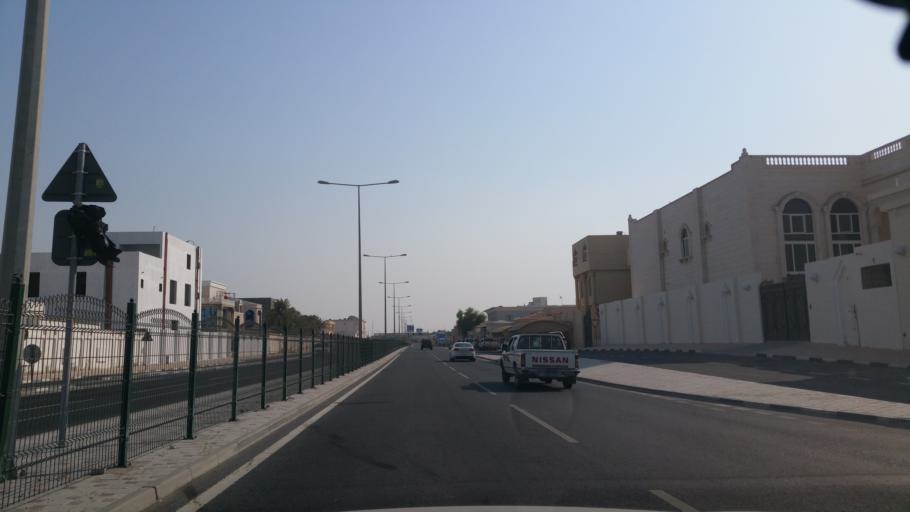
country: QA
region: Baladiyat ar Rayyan
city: Ar Rayyan
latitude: 25.3163
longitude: 51.4086
